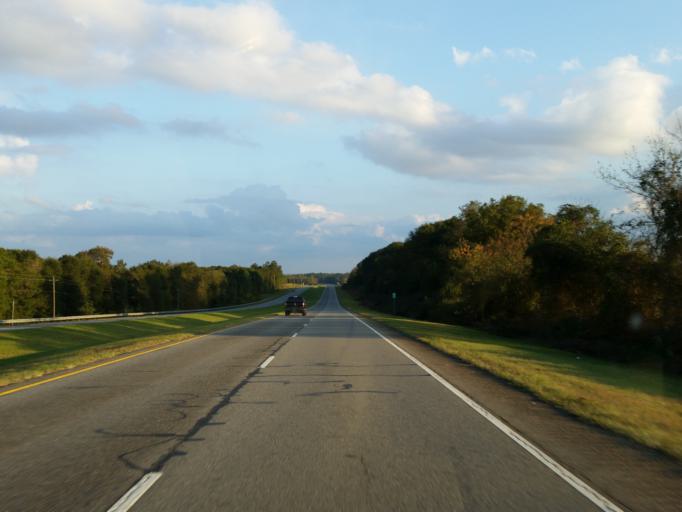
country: US
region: Georgia
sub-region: Houston County
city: Perry
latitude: 32.4377
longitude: -83.7264
